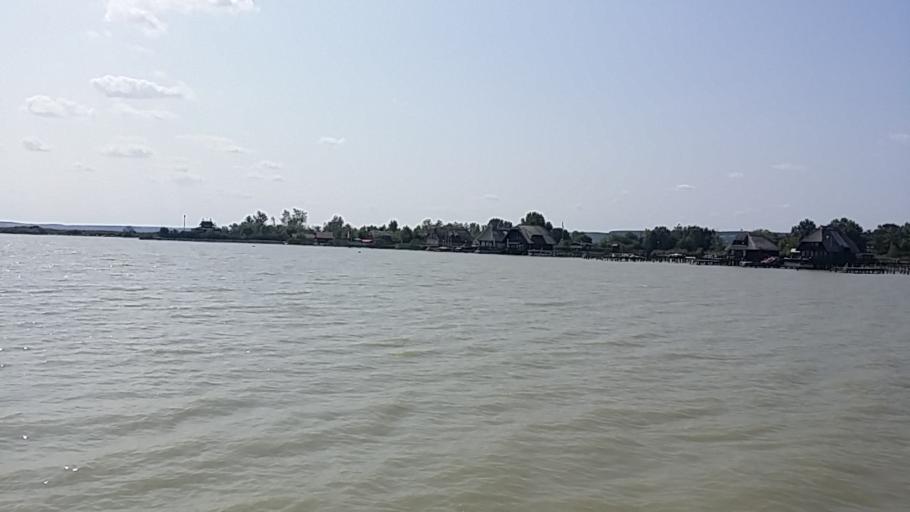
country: AT
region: Burgenland
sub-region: Eisenstadt-Umgebung
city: Morbisch am See
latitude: 47.7242
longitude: 16.6934
